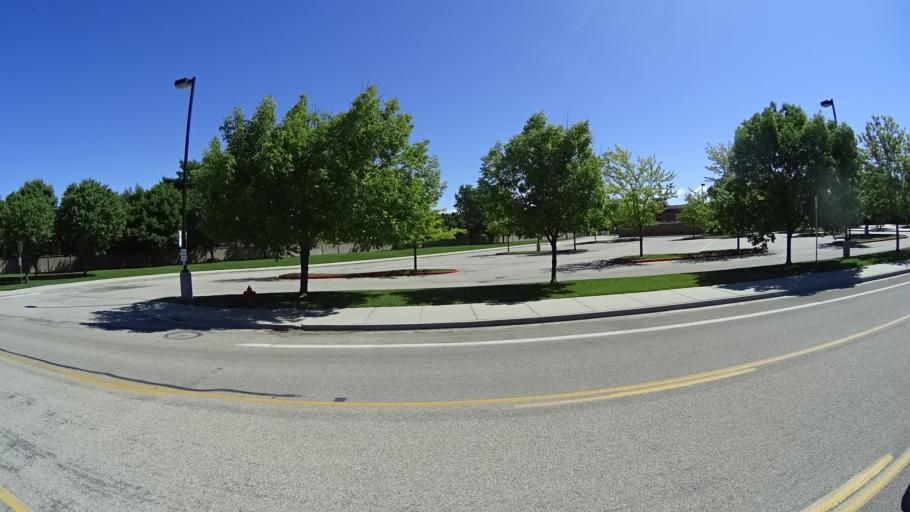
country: US
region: Idaho
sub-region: Ada County
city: Meridian
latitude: 43.6406
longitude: -116.3702
